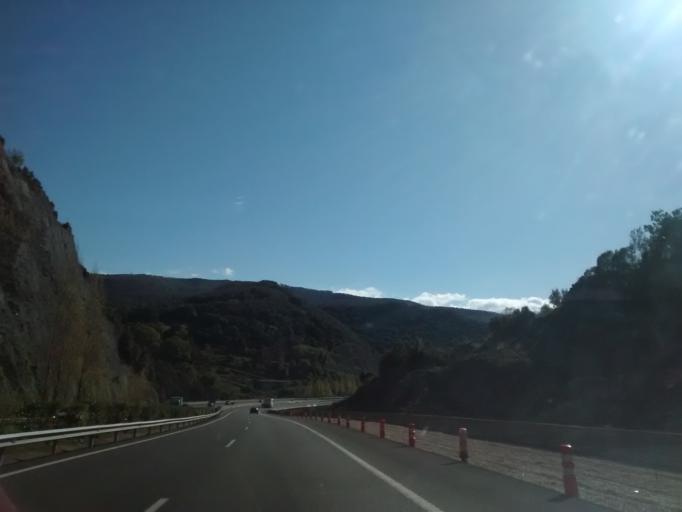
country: ES
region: Cantabria
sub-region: Provincia de Cantabria
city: Liendo
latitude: 43.3846
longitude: -3.3643
